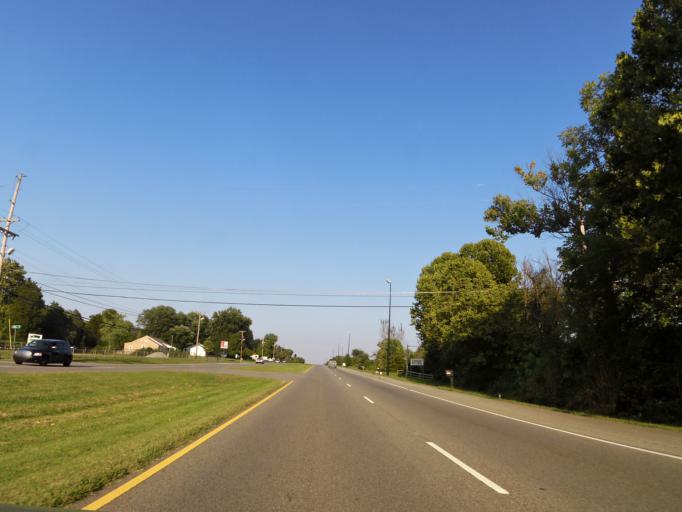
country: US
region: Tennessee
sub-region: Knox County
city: Mascot
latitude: 36.0187
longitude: -83.8050
